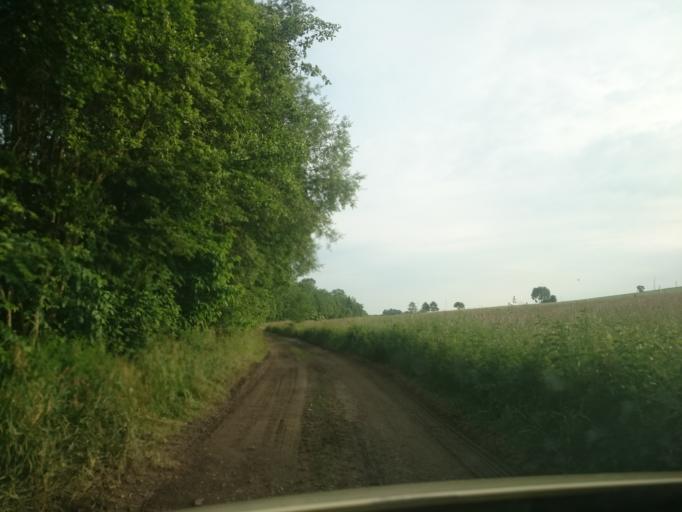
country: DE
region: Saxony
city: Eppendorf
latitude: 50.8336
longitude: 13.2389
